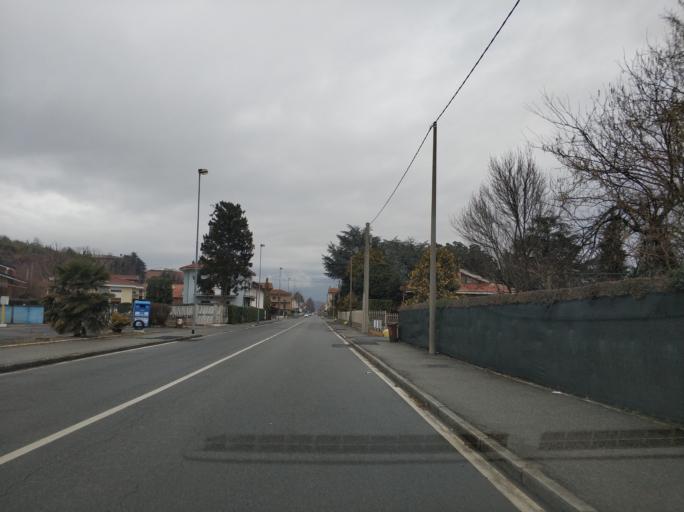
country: IT
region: Piedmont
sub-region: Provincia di Torino
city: Banchette
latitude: 45.4427
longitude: 7.8777
